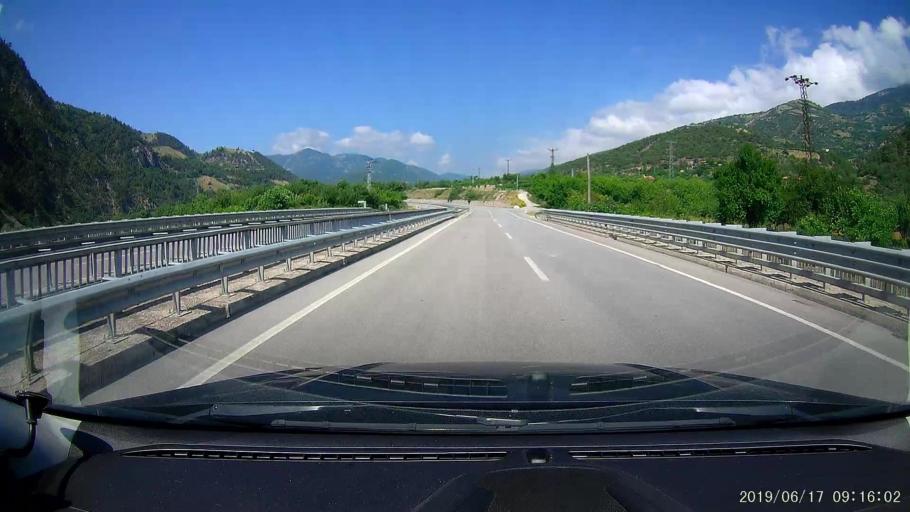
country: TR
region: Amasya
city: Akdag
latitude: 40.7463
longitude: 36.0219
